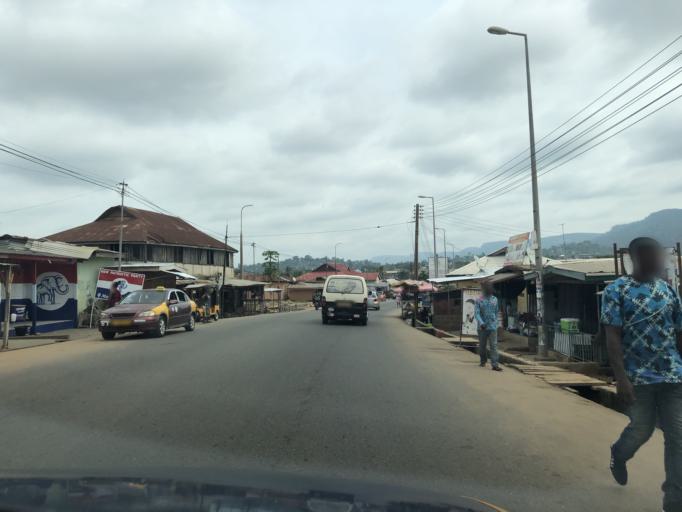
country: GH
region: Eastern
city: Koforidua
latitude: 6.1100
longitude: -0.2687
